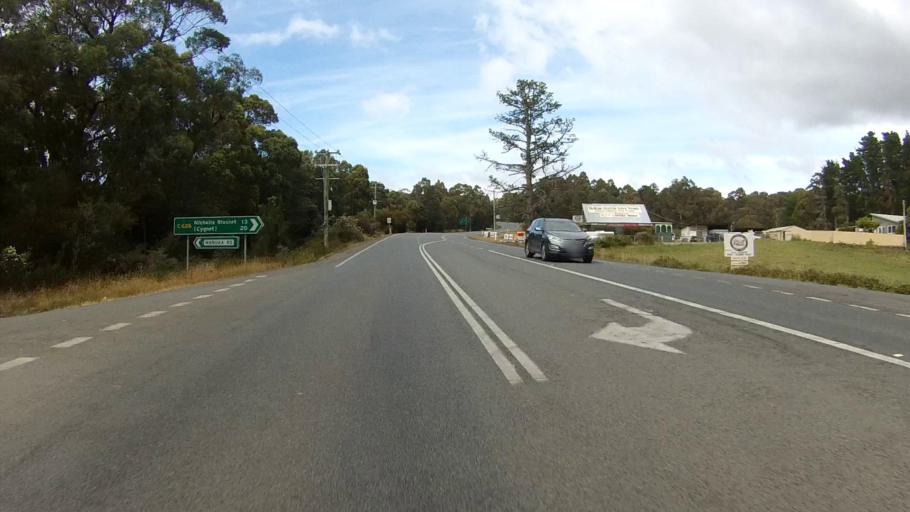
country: AU
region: Tasmania
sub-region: Kingborough
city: Kettering
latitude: -43.1065
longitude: 147.2447
